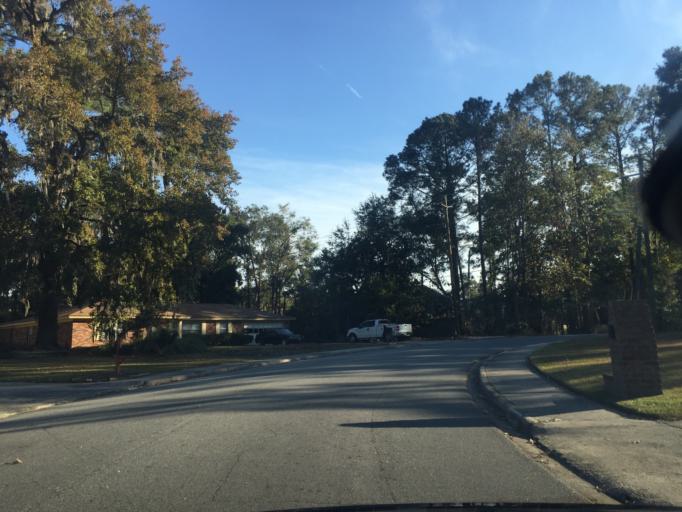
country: US
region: Georgia
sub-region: Chatham County
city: Montgomery
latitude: 31.9926
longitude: -81.1353
